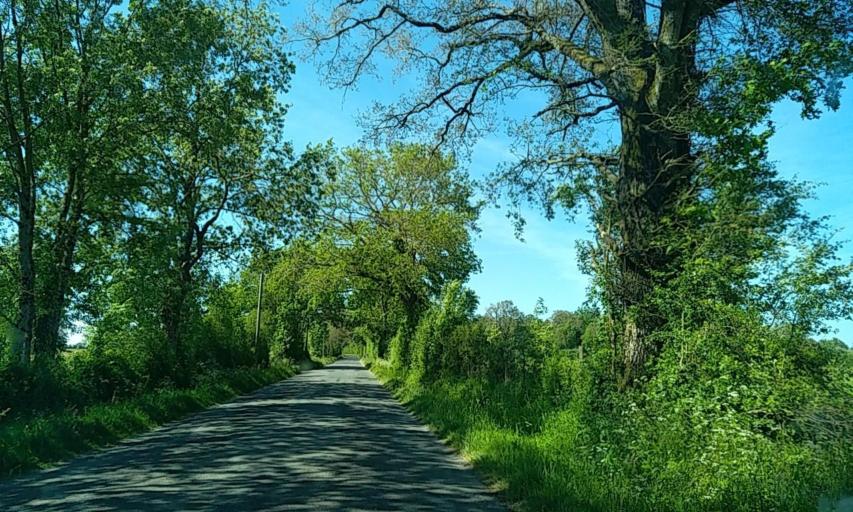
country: FR
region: Poitou-Charentes
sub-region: Departement des Deux-Sevres
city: Boisme
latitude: 46.7957
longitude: -0.4528
